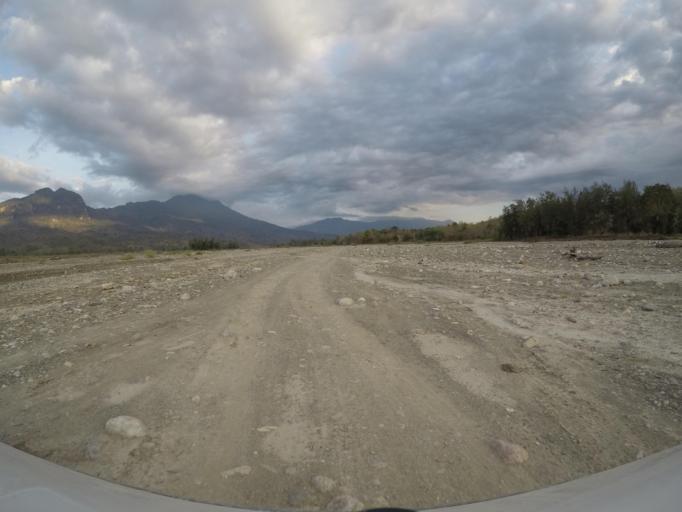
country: TL
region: Bobonaro
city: Maliana
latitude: -8.9051
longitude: 125.2102
